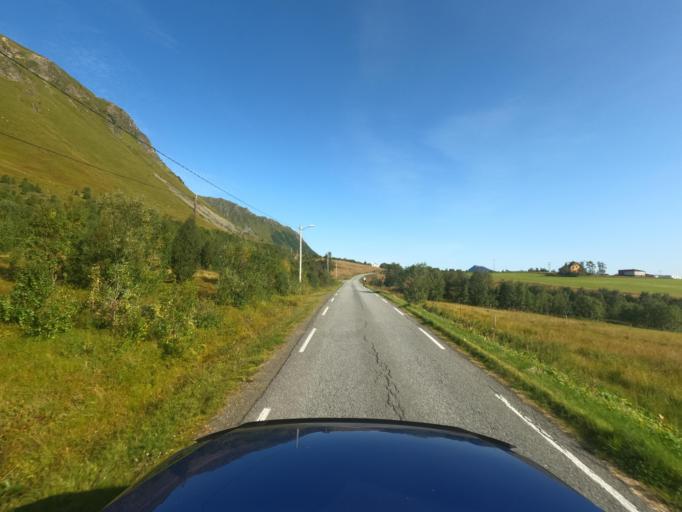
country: NO
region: Nordland
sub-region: Vestvagoy
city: Evjen
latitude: 68.2847
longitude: 13.9915
